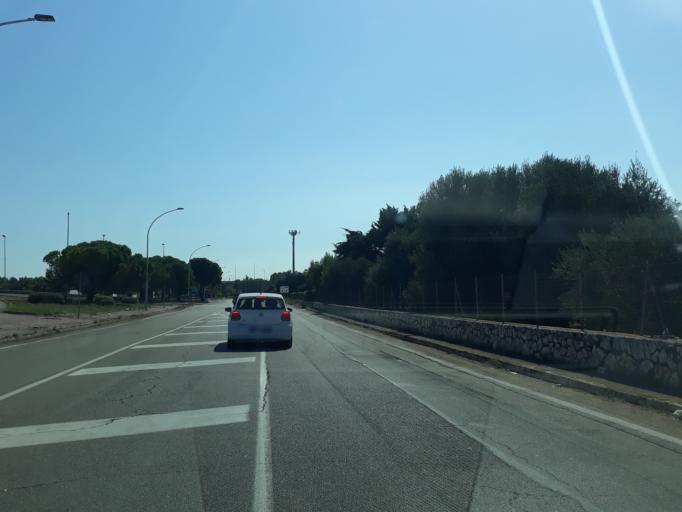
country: IT
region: Apulia
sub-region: Provincia di Bari
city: Monopoli
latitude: 40.9260
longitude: 17.3143
